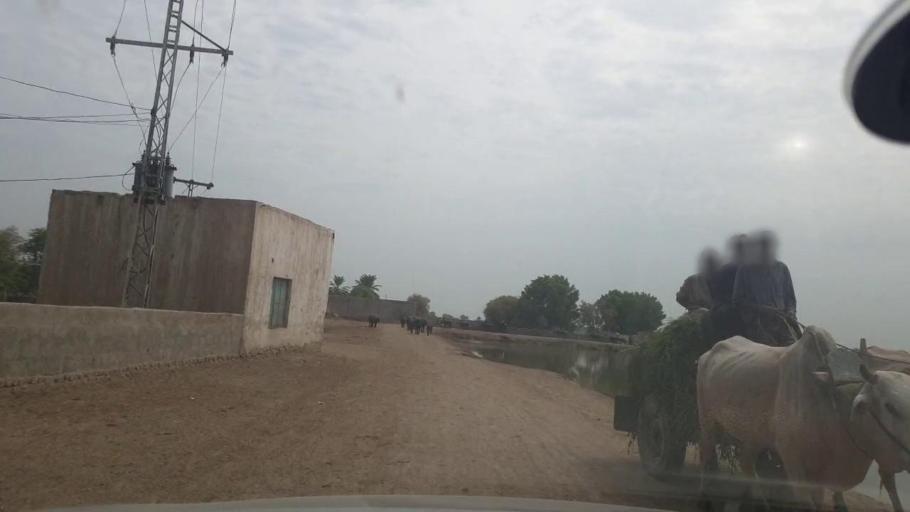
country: PK
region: Sindh
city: Jacobabad
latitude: 28.2413
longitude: 68.5392
